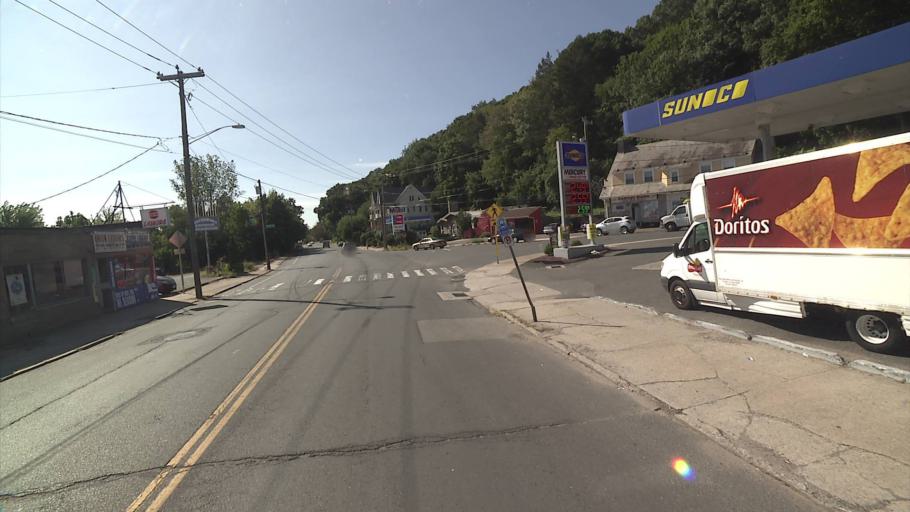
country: US
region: Connecticut
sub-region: New Haven County
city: Waterbury
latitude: 41.5649
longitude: -73.0595
